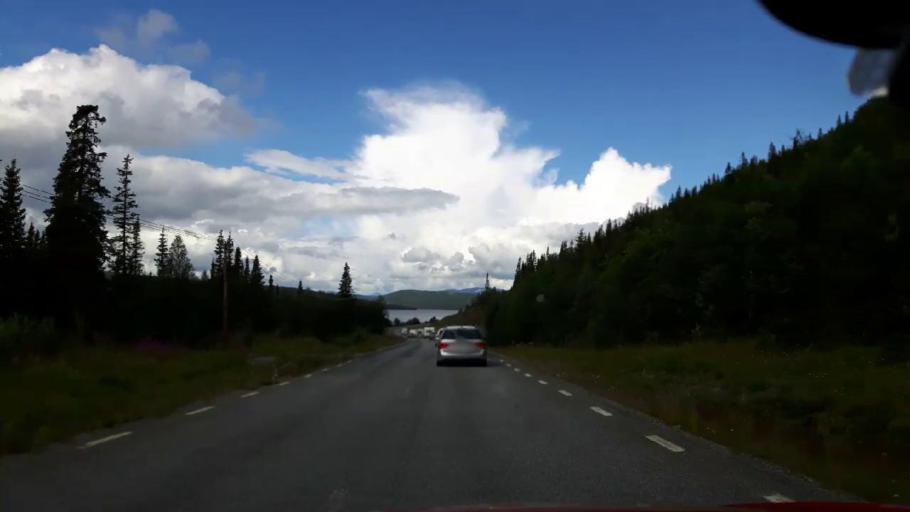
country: SE
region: Vaesterbotten
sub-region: Vilhelmina Kommun
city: Sjoberg
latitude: 65.0379
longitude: 15.1270
